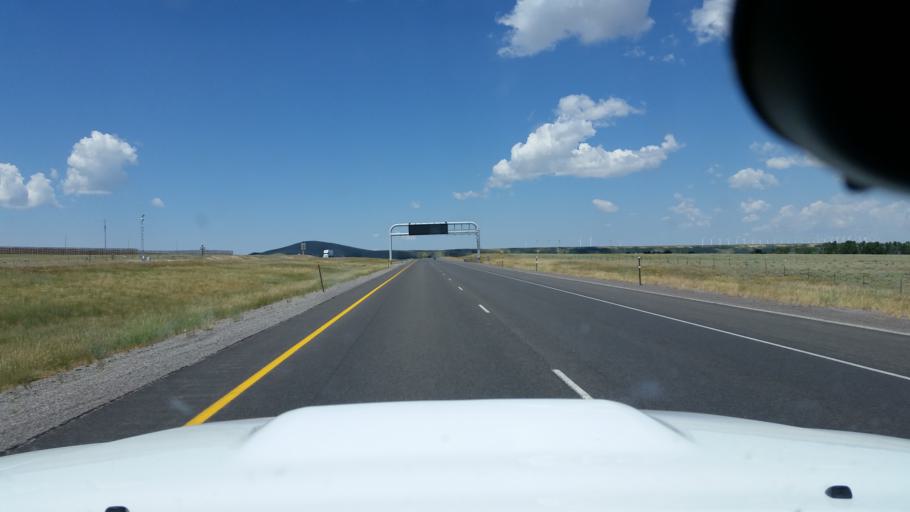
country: US
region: Wyoming
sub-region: Carbon County
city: Saratoga
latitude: 41.5866
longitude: -106.1769
